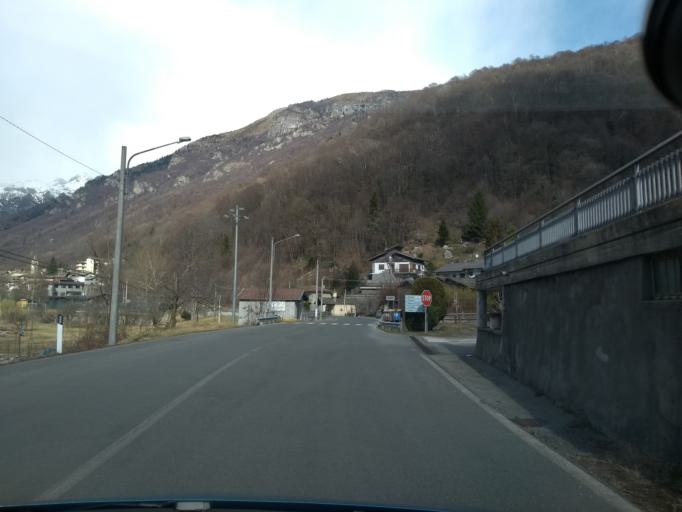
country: IT
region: Piedmont
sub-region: Provincia di Torino
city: Chialamberto
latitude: 45.3608
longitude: 7.3508
